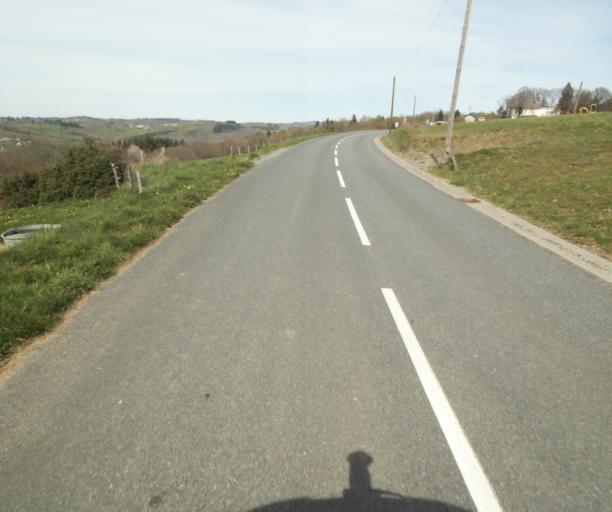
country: FR
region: Limousin
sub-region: Departement de la Correze
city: Naves
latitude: 45.3648
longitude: 1.7951
